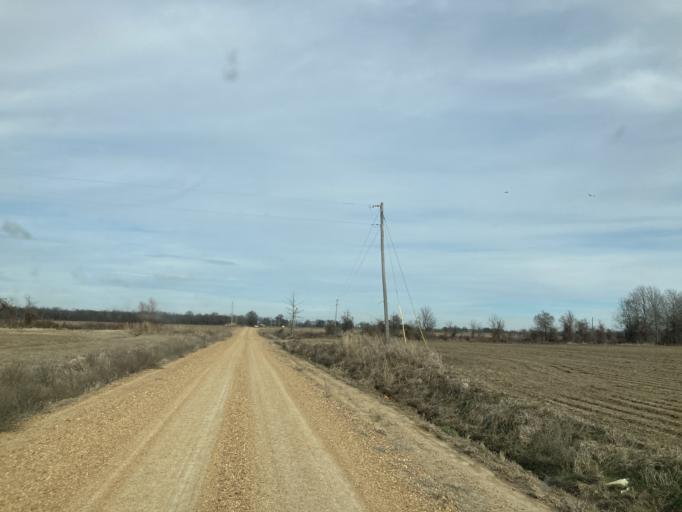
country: US
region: Mississippi
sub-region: Humphreys County
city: Belzoni
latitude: 33.0581
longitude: -90.6577
